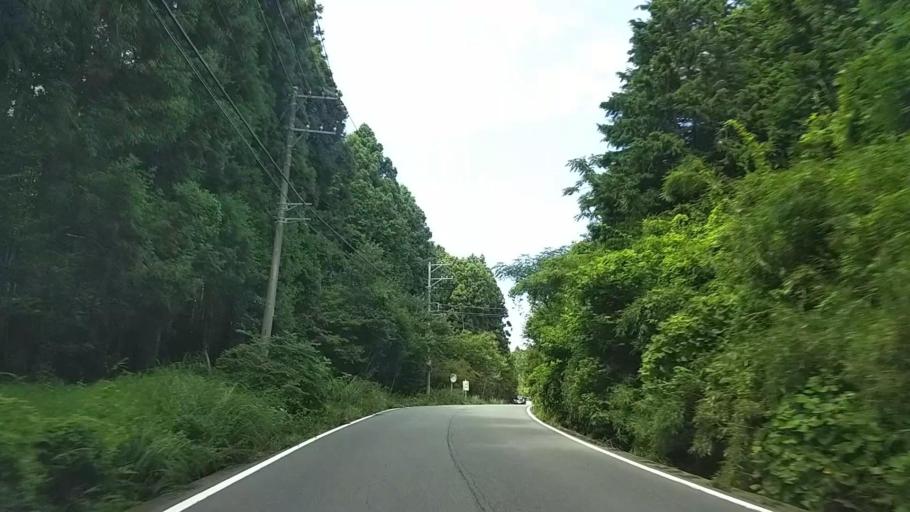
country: JP
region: Shizuoka
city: Gotemba
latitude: 35.2432
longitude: 138.8648
